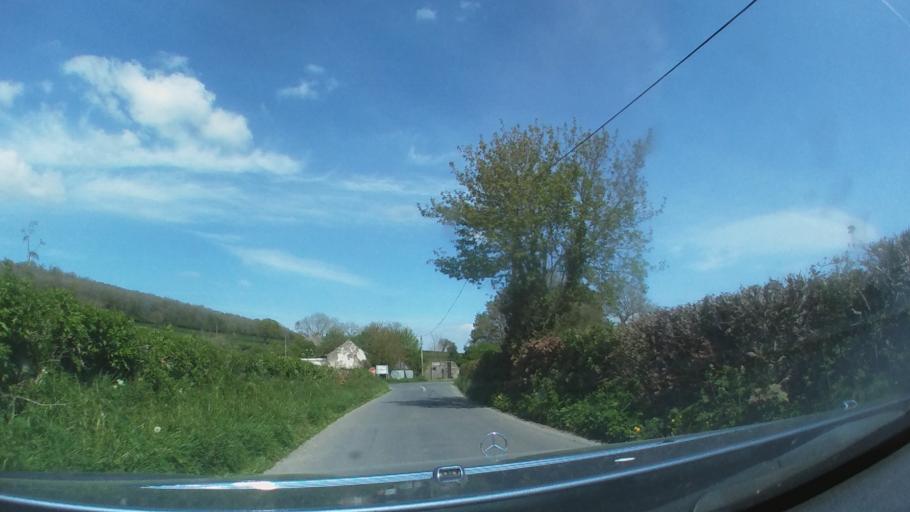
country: IE
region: Leinster
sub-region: Kilkenny
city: Callan
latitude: 52.6051
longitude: -7.3907
